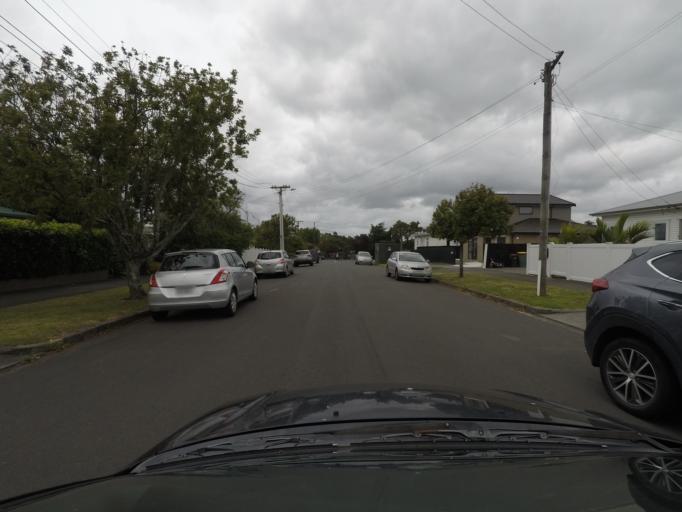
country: NZ
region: Auckland
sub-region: Auckland
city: Rosebank
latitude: -36.8676
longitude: 174.7019
